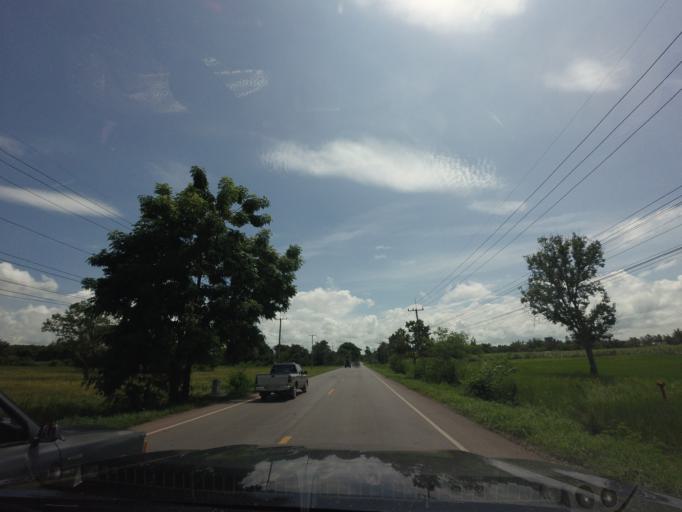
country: TH
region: Changwat Udon Thani
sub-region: Amphoe Ban Phue
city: Ban Phue
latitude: 17.7068
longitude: 102.4264
